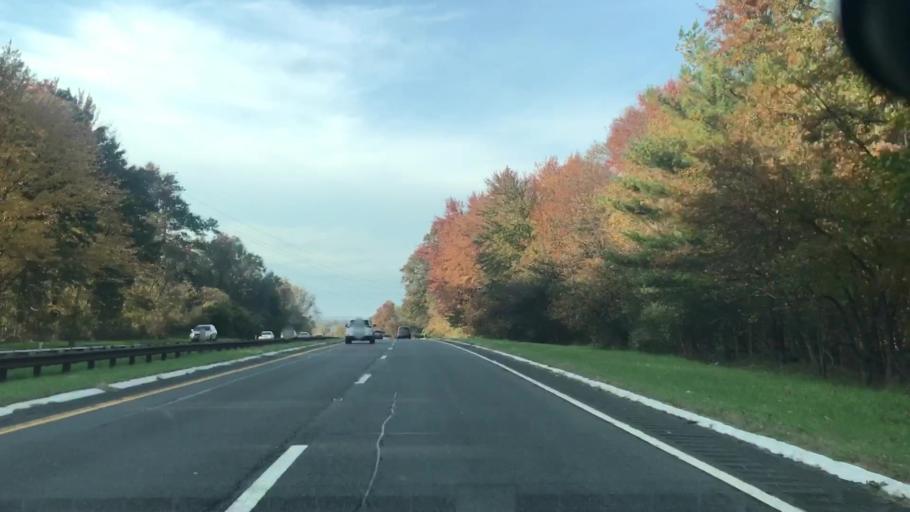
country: US
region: New York
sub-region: Rockland County
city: Blauvelt
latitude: 41.0518
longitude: -73.9619
